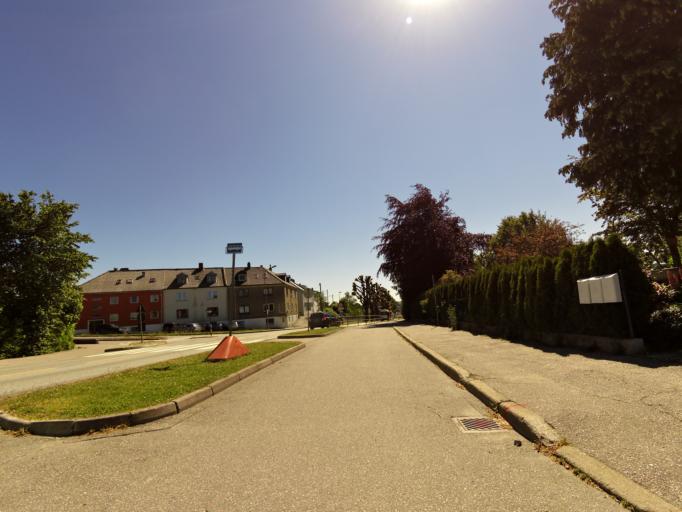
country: NO
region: Vest-Agder
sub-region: Kristiansand
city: Kristiansand
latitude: 58.1554
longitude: 8.0103
